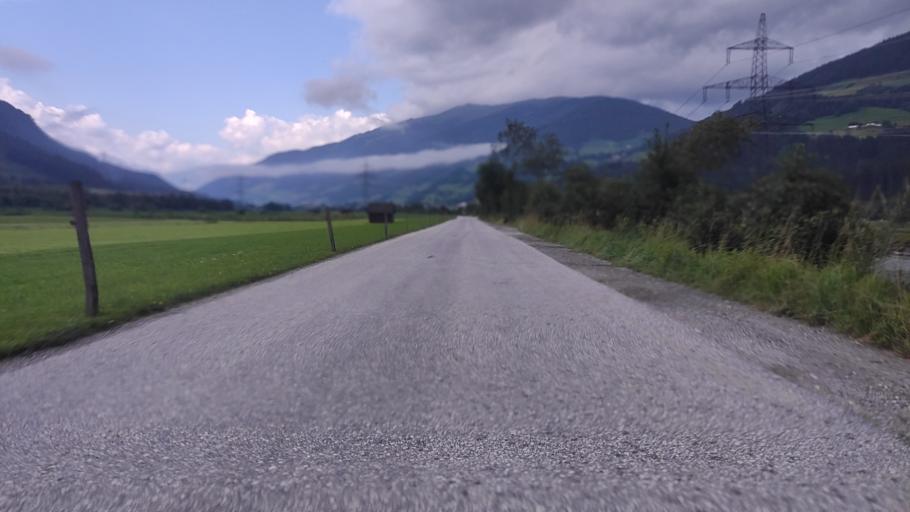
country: AT
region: Salzburg
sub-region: Politischer Bezirk Zell am See
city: Hollersbach im Pinzgau
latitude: 47.2787
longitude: 12.4070
